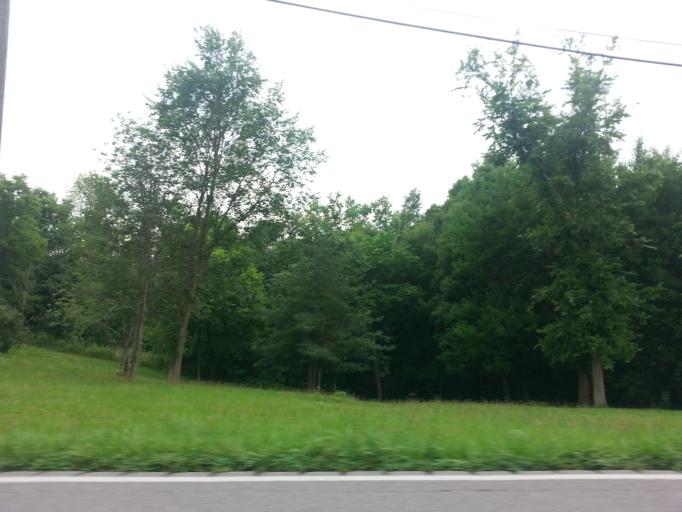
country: US
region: Kentucky
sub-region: Robertson County
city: Mount Olivet
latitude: 38.5341
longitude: -84.0251
